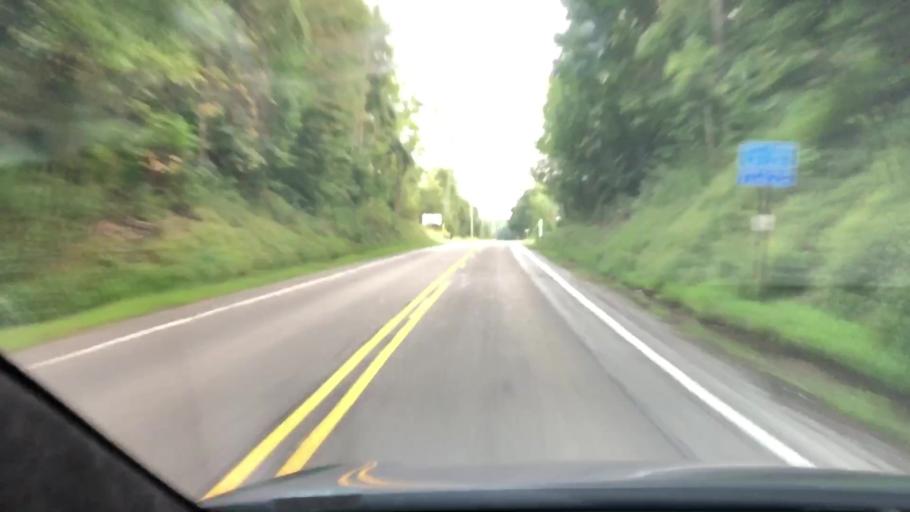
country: US
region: Pennsylvania
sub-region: Butler County
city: Slippery Rock
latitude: 41.0893
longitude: -80.0018
